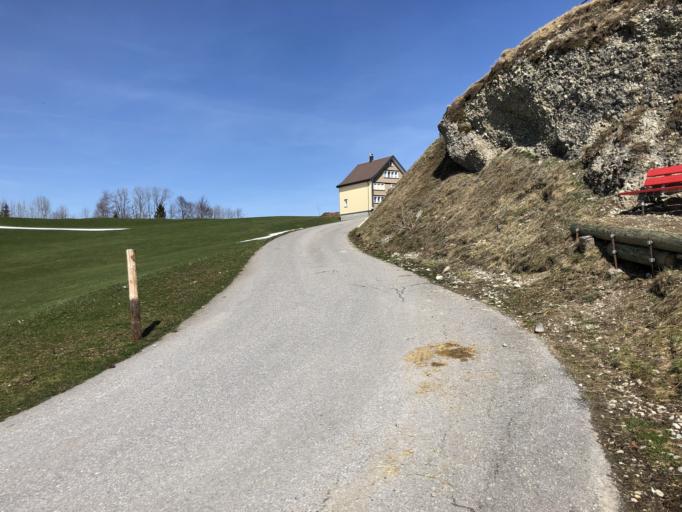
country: CH
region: Appenzell Innerrhoden
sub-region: Appenzell Inner Rhodes
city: Gonten
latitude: 47.3413
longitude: 9.3690
